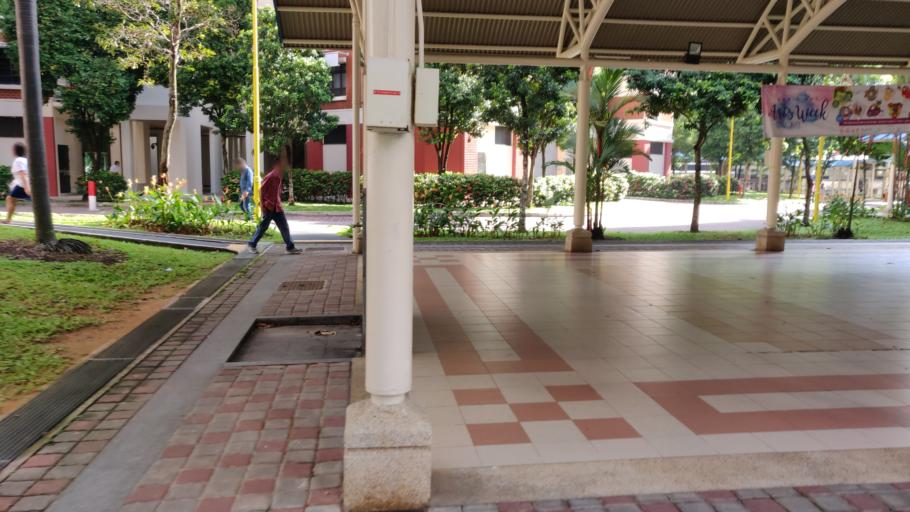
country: SG
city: Singapore
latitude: 1.2885
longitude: 103.8162
